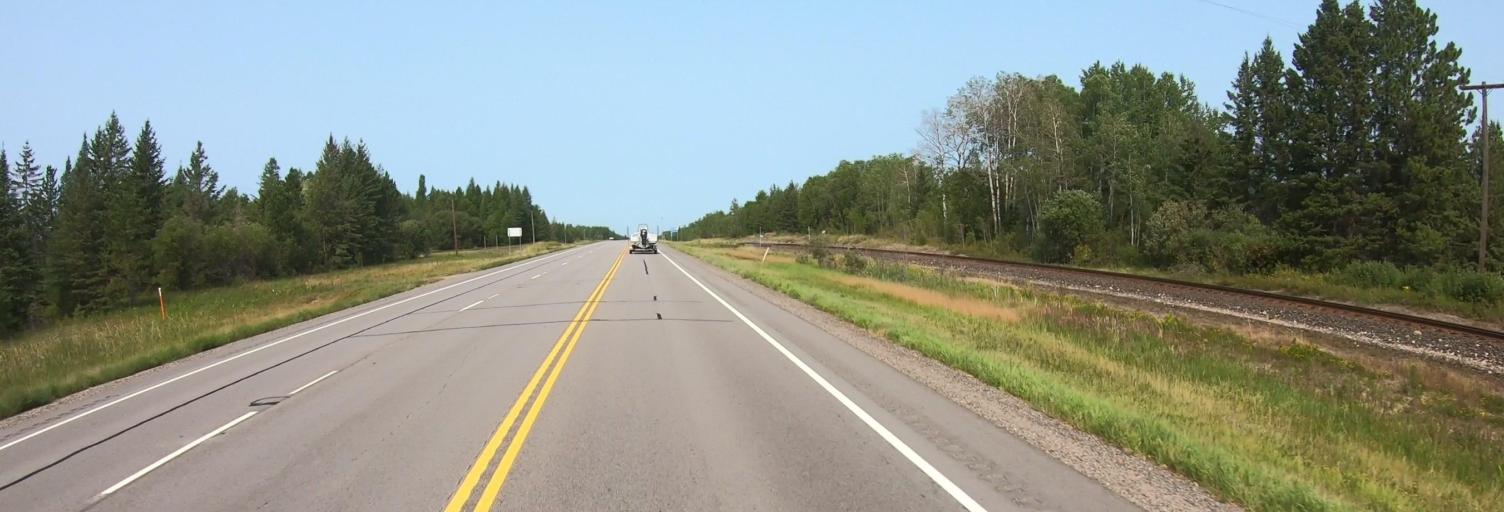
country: CA
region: Ontario
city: Fort Frances
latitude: 48.4444
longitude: -93.2612
